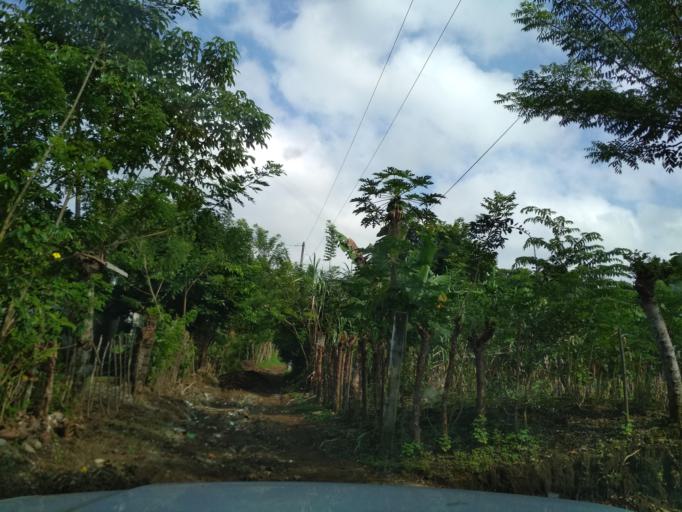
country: MX
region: Veracruz
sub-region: San Andres Tuxtla
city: Matacapan
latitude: 18.4423
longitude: -95.1737
